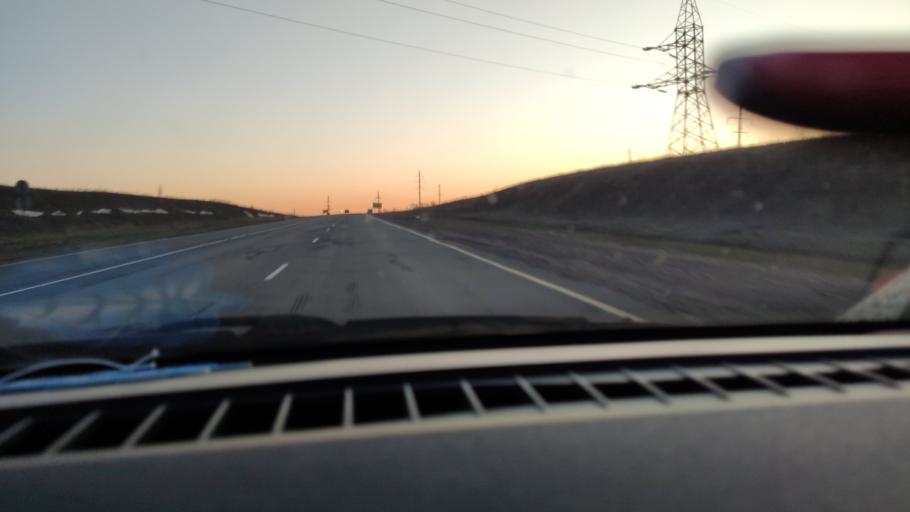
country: RU
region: Saratov
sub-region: Saratovskiy Rayon
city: Saratov
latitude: 51.7666
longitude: 46.0788
